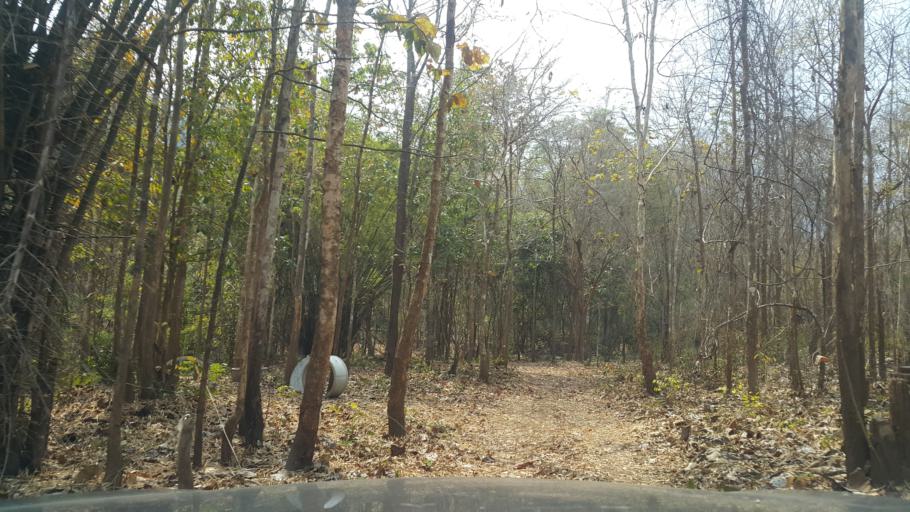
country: TH
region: Lampang
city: Sop Prap
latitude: 17.9315
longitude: 99.2352
